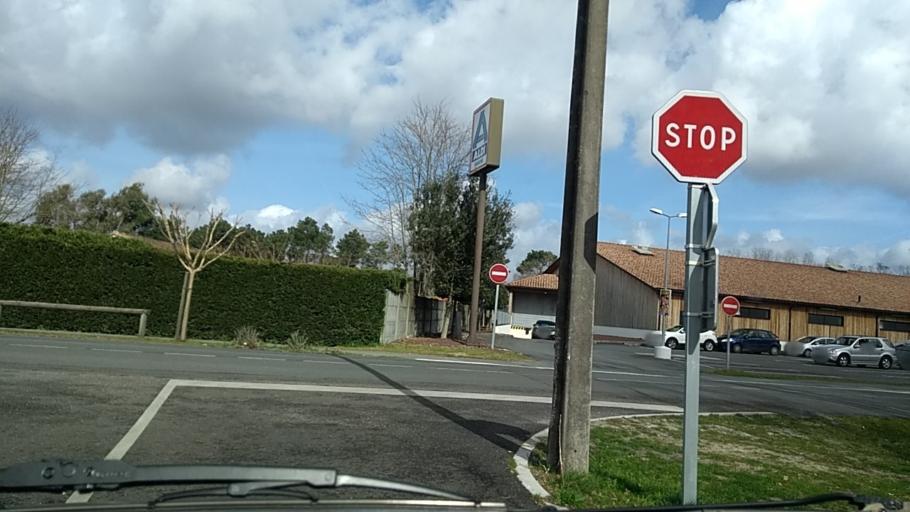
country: FR
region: Aquitaine
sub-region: Departement de la Gironde
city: Salles
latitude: 44.5478
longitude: -0.8772
